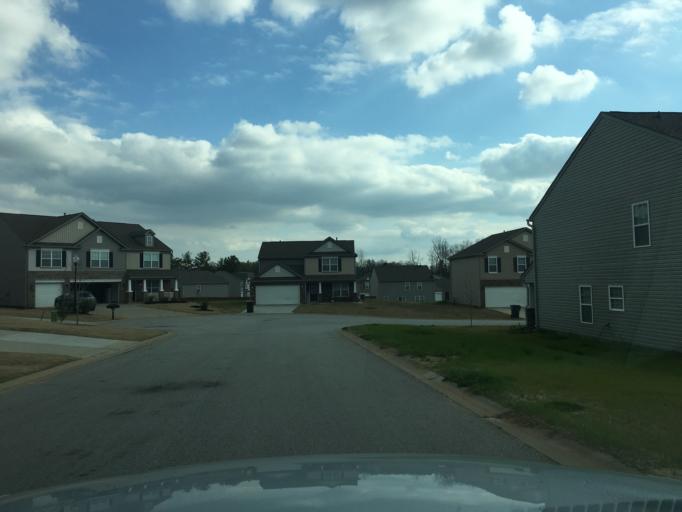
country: US
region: South Carolina
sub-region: Spartanburg County
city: Duncan
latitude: 34.8934
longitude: -82.1246
